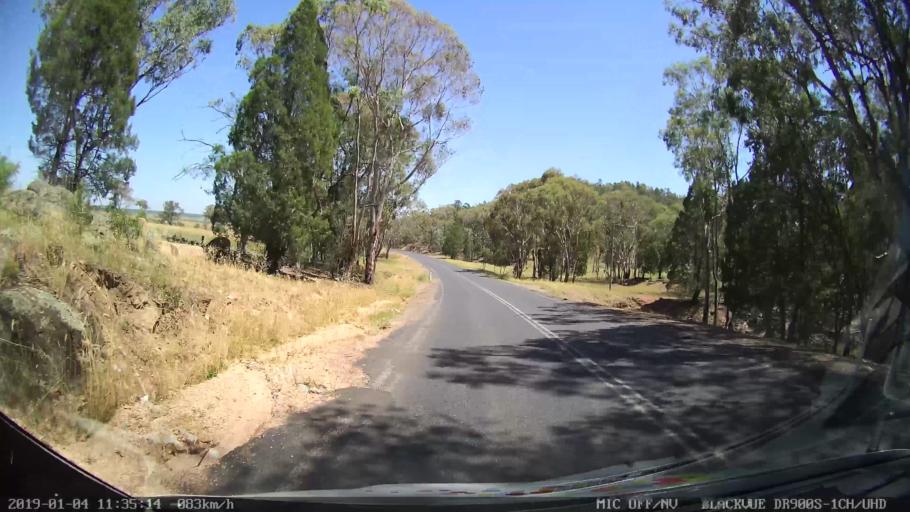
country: AU
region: New South Wales
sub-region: Cabonne
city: Molong
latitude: -33.0577
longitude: 148.8228
